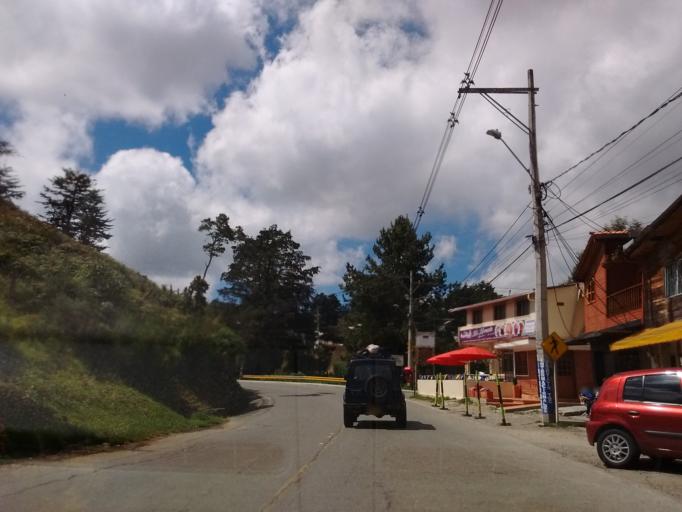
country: CO
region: Antioquia
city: Medellin
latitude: 6.2125
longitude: -75.5021
